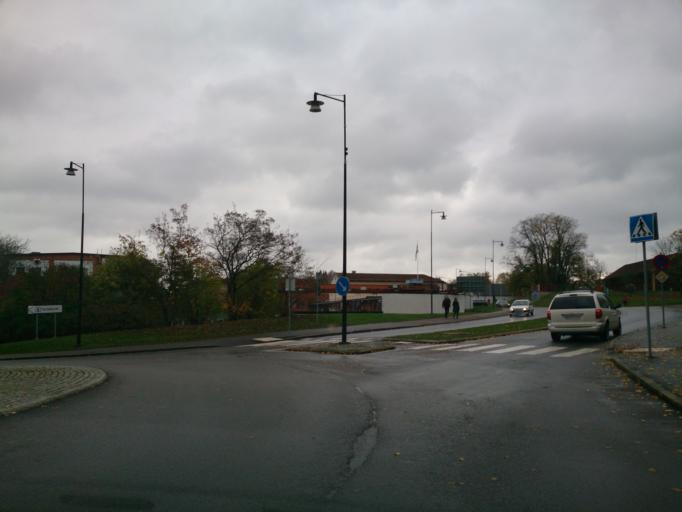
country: SE
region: OEstergoetland
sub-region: Atvidabergs Kommun
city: Atvidaberg
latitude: 58.1993
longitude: 16.0005
